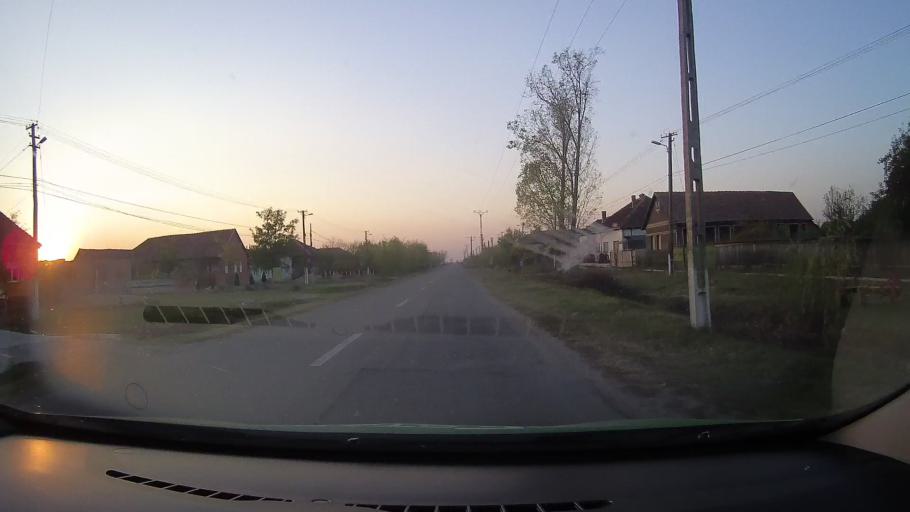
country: RO
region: Arad
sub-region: Comuna Zarand
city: Zarand
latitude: 46.4078
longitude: 21.6377
